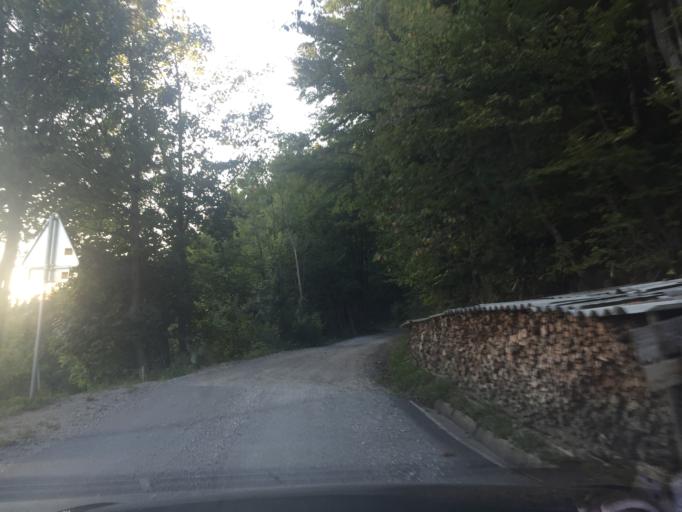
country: SI
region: Sostanj
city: Topolsica
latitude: 46.4538
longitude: 14.9928
